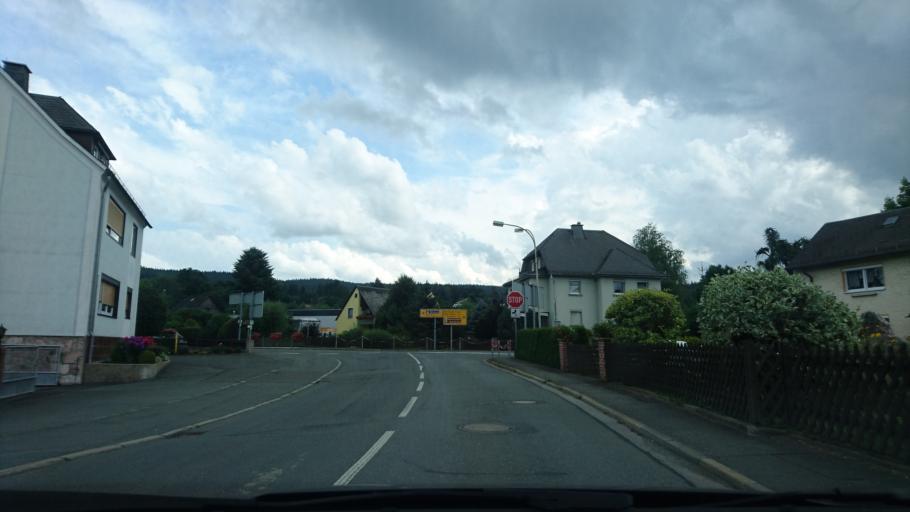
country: DE
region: Bavaria
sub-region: Upper Franconia
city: Lichtenberg
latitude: 50.3572
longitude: 11.6838
